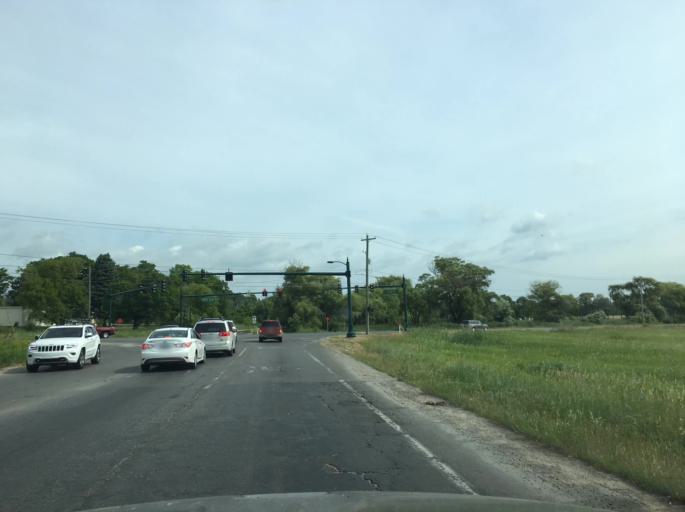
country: US
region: Michigan
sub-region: Grand Traverse County
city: Traverse City
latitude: 44.7468
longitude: -85.6453
